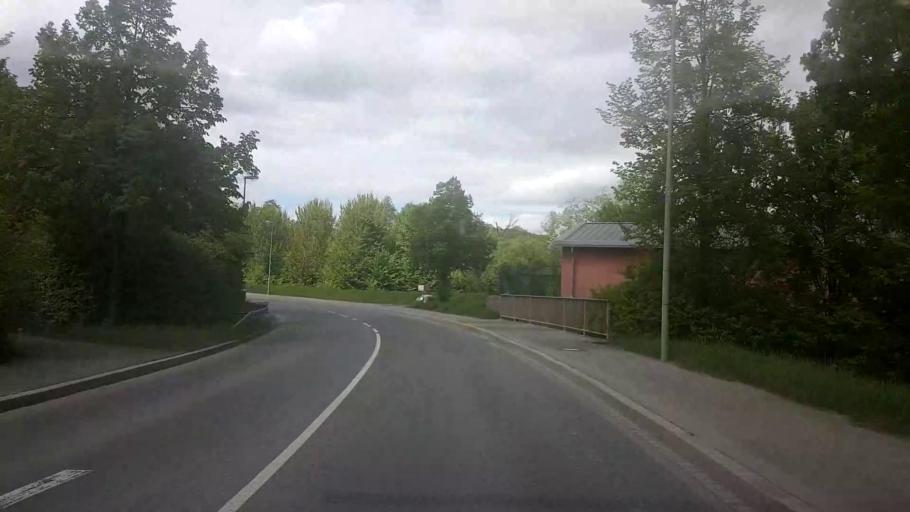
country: DE
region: Bavaria
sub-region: Upper Franconia
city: Lichtenfels
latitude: 50.1518
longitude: 11.0652
